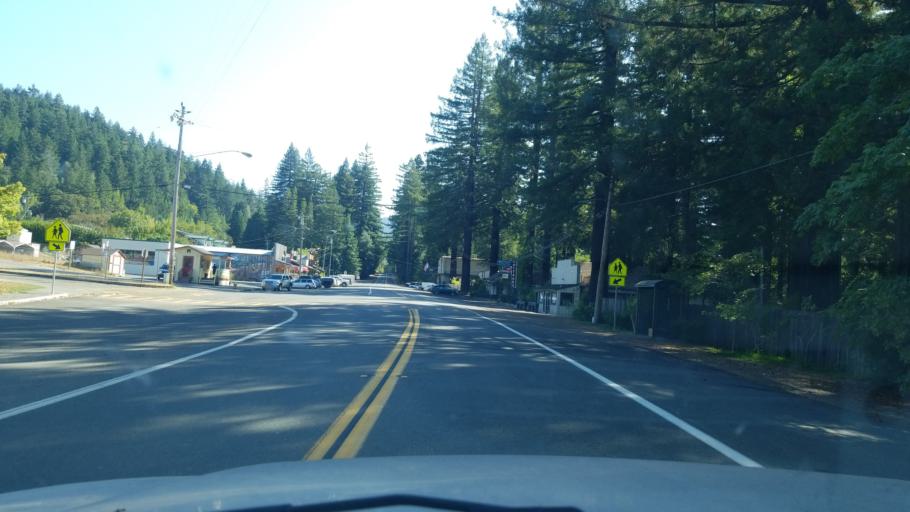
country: US
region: California
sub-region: Humboldt County
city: Redway
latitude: 40.2370
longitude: -123.8244
